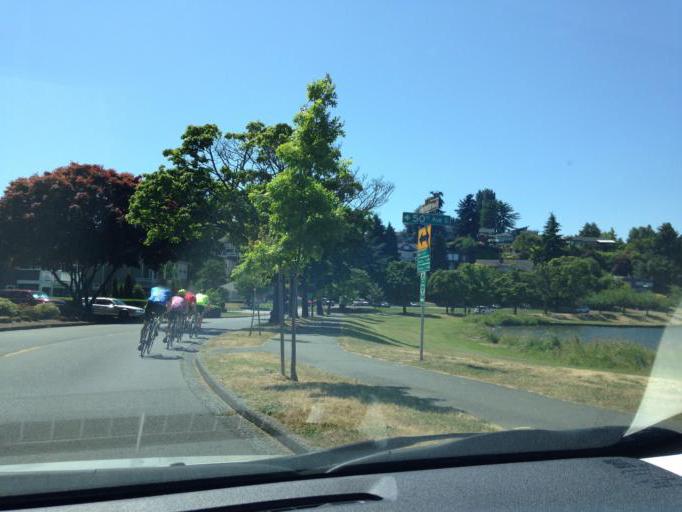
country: US
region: Washington
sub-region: King County
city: Mercer Island
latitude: 47.5678
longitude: -122.2706
